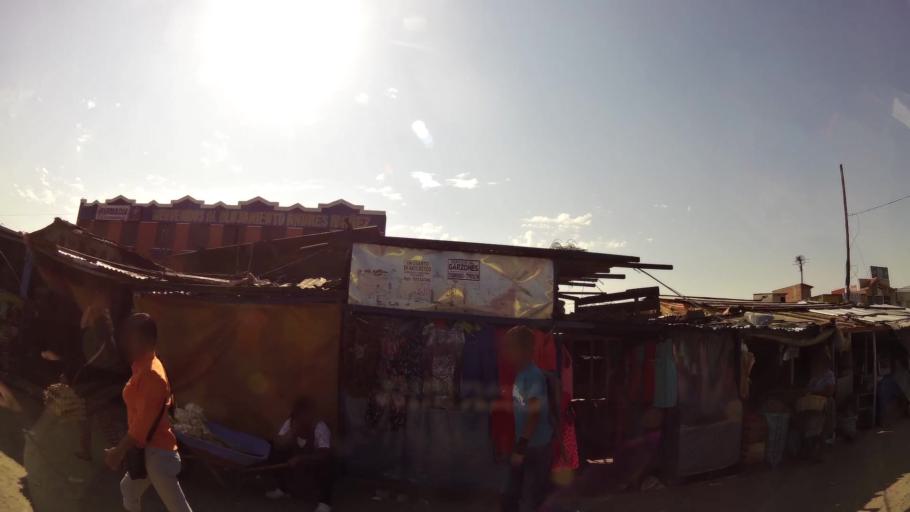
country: BO
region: Santa Cruz
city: Santa Cruz de la Sierra
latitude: -17.8248
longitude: -63.1314
